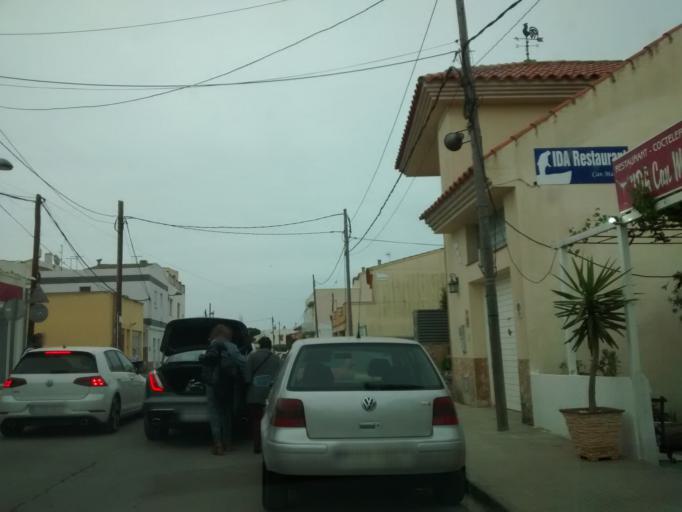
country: ES
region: Catalonia
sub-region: Provincia de Tarragona
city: Deltebre
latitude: 40.6695
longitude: 0.7543
